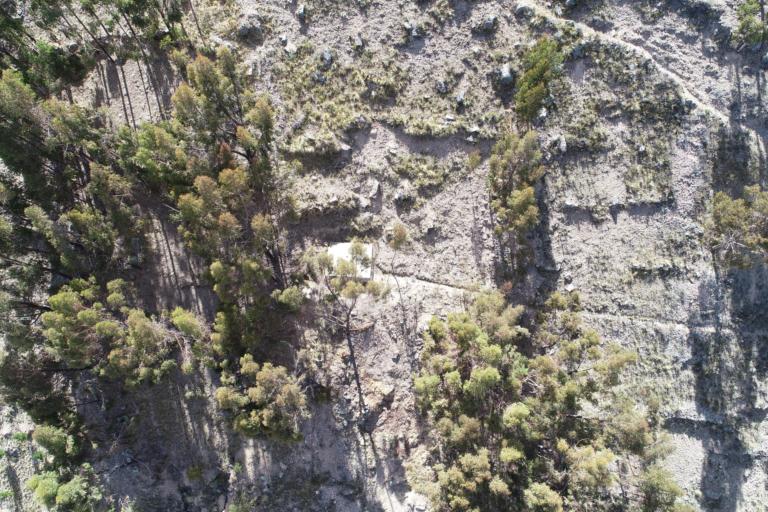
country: BO
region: La Paz
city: Achacachi
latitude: -15.8933
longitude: -68.9073
